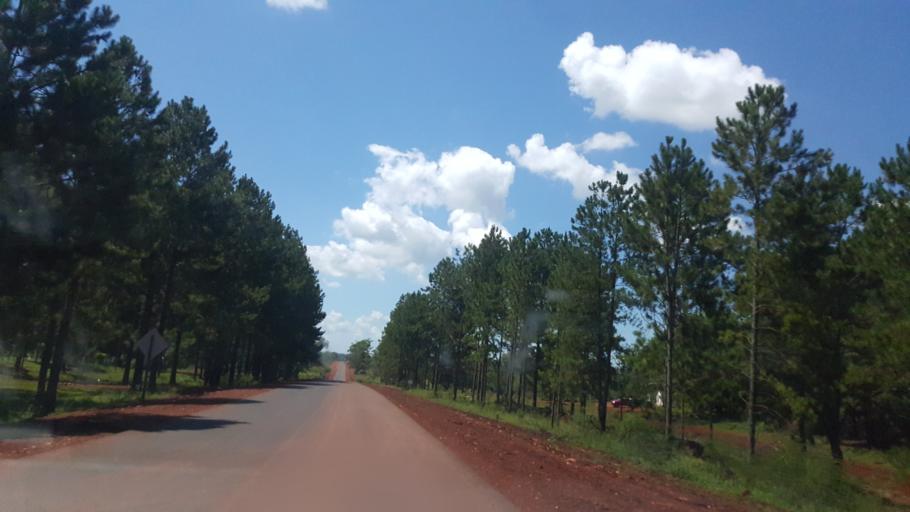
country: AR
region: Corrientes
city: Santo Tome
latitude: -28.5120
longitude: -56.0597
